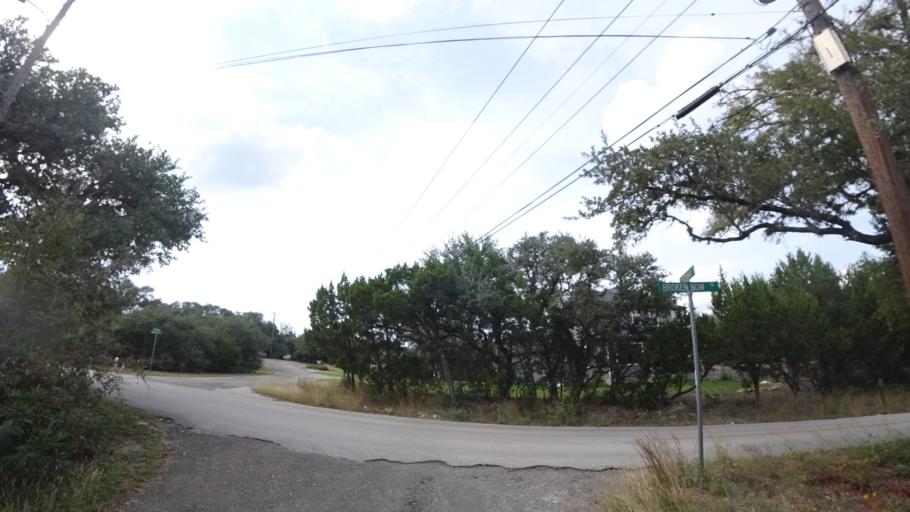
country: US
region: Texas
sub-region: Travis County
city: Hudson Bend
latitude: 30.3870
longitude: -97.9250
